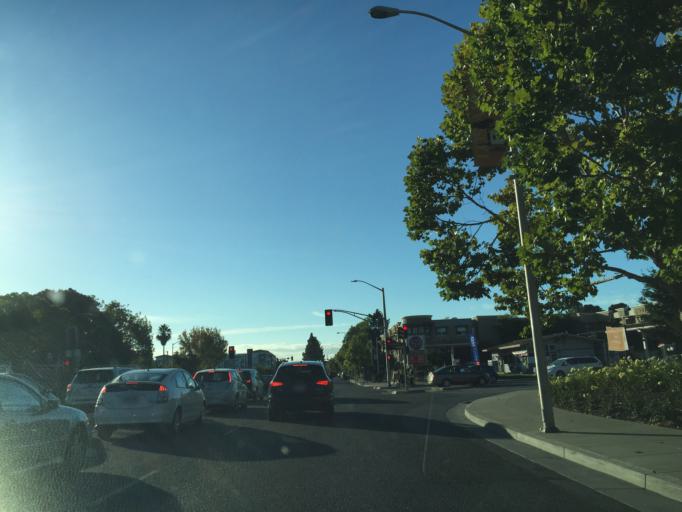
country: US
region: California
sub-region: Santa Clara County
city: Los Altos
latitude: 37.4050
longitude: -122.1188
